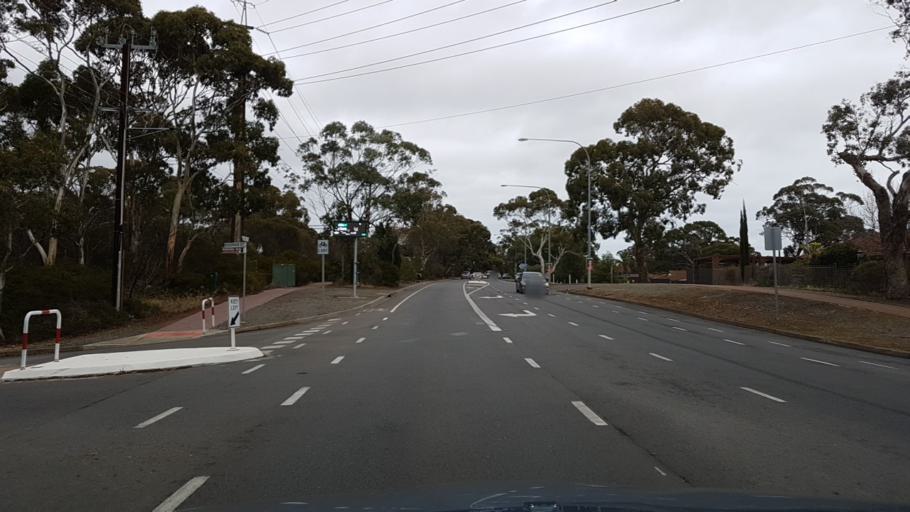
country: AU
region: South Australia
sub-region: Onkaparinga
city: Bedford Park
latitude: -35.0502
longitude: 138.5794
